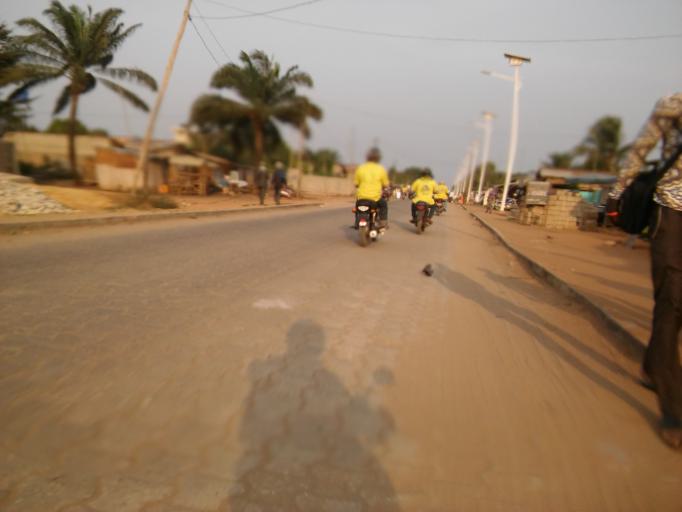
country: BJ
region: Atlantique
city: Abomey-Calavi
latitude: 6.4022
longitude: 2.3299
